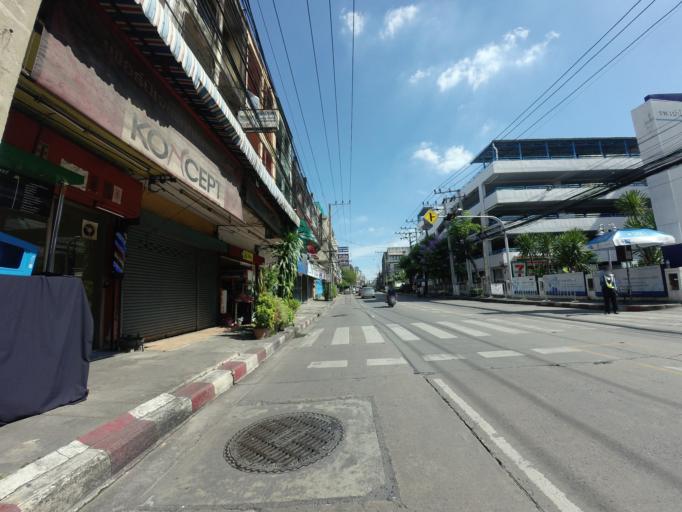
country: TH
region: Bangkok
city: Lat Phrao
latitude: 13.8019
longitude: 100.5964
